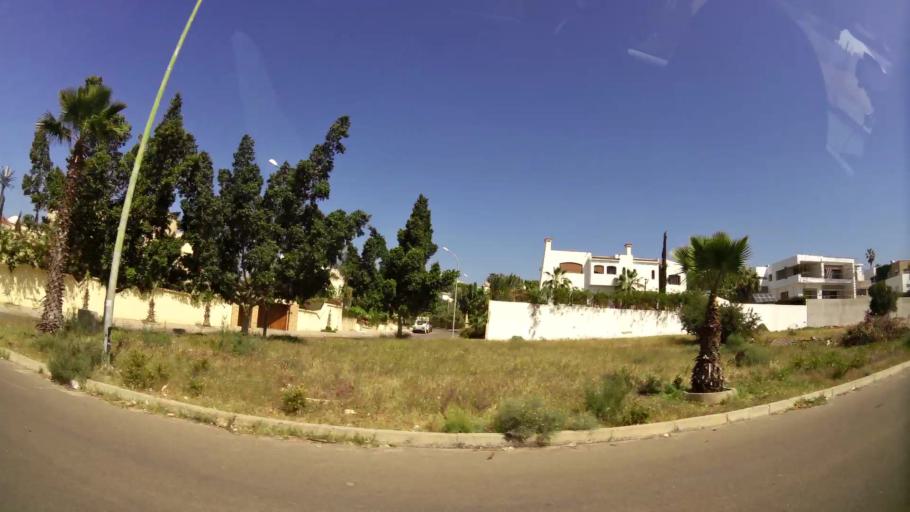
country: MA
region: Souss-Massa-Draa
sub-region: Agadir-Ida-ou-Tnan
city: Agadir
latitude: 30.4409
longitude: -9.5889
